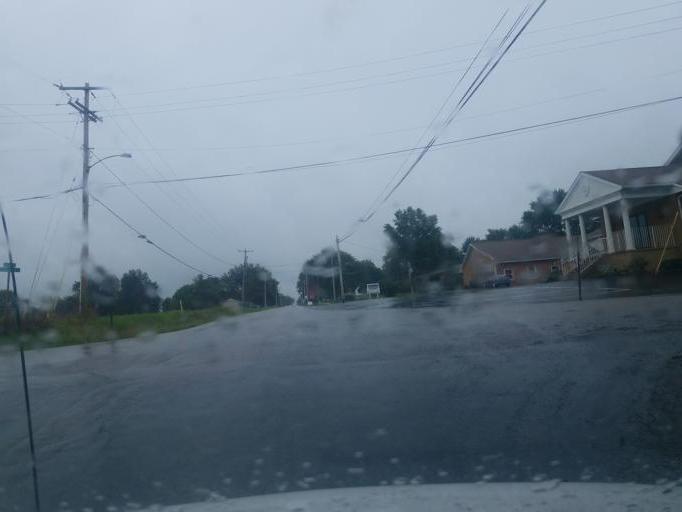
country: US
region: Ohio
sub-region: Wayne County
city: Rittman
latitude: 40.9778
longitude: -81.8012
